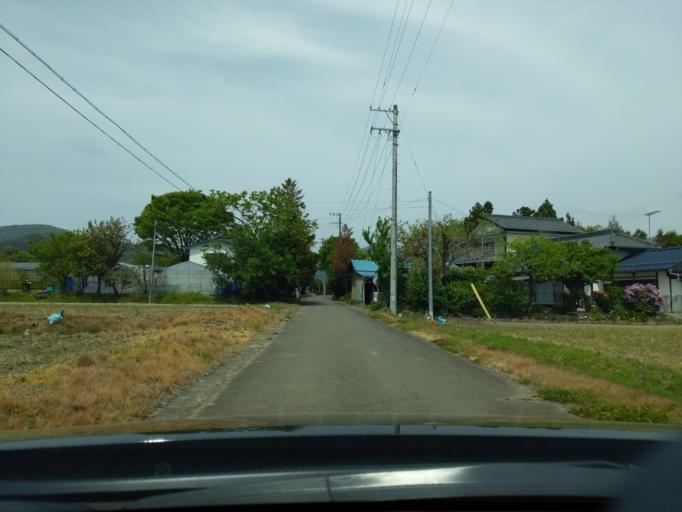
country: JP
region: Fukushima
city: Koriyama
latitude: 37.4065
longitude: 140.2585
